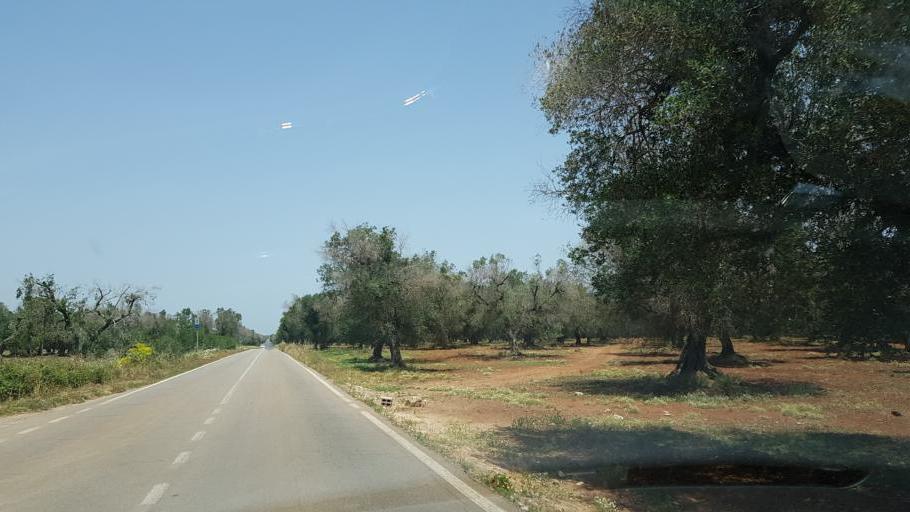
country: IT
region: Apulia
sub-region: Provincia di Lecce
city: Veglie
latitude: 40.3082
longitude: 17.9196
